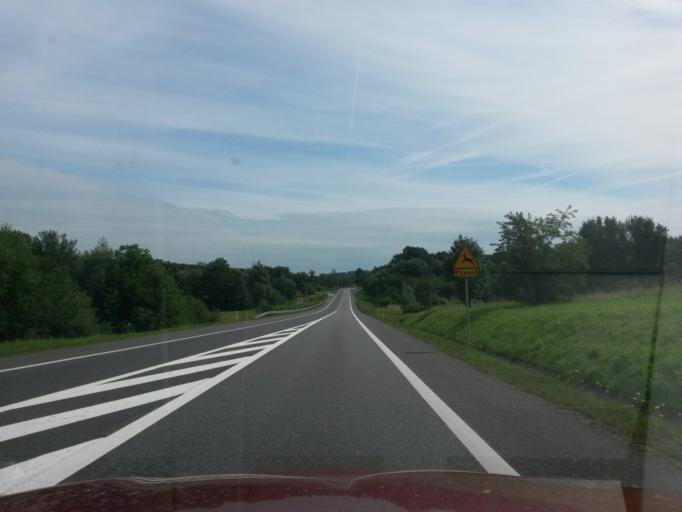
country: PL
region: Lesser Poland Voivodeship
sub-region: Powiat bochenski
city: Stanislawice
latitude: 49.9631
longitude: 20.3503
